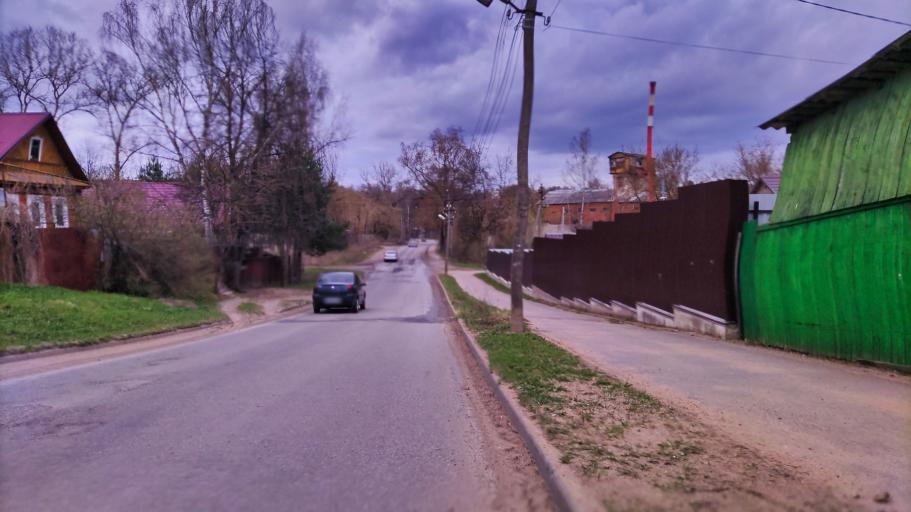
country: RU
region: Tverskaya
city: Rzhev
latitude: 56.2558
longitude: 34.3359
